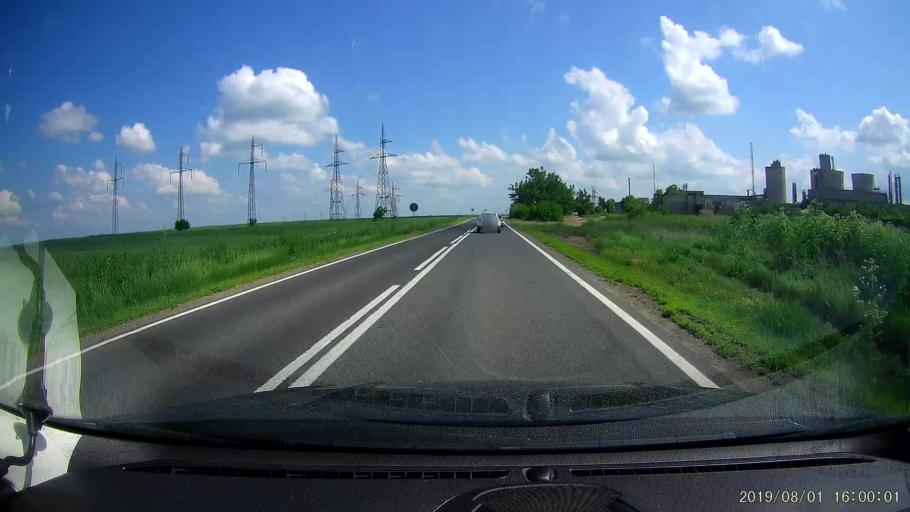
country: RO
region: Ialomita
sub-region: Comuna Slobozia
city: Slobozia
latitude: 44.5367
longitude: 27.3877
